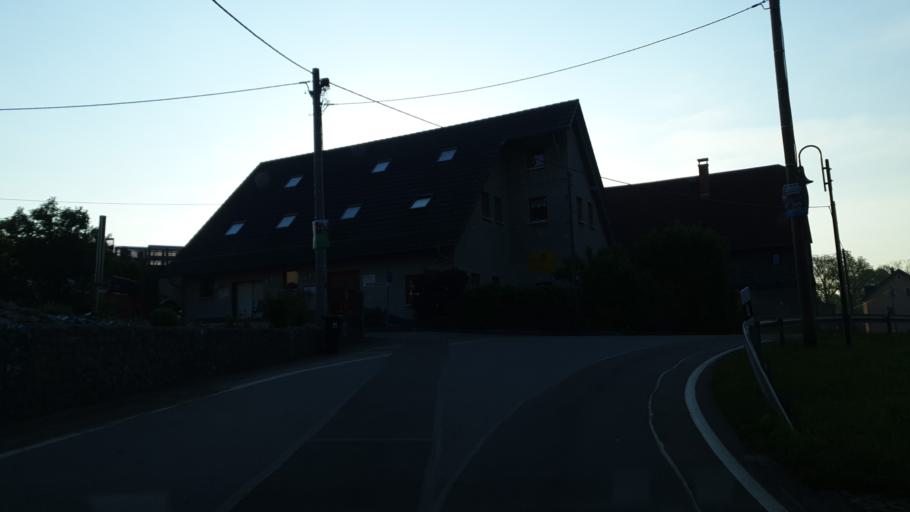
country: DE
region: Saxony
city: Bernsdorf
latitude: 50.7844
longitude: 12.6754
